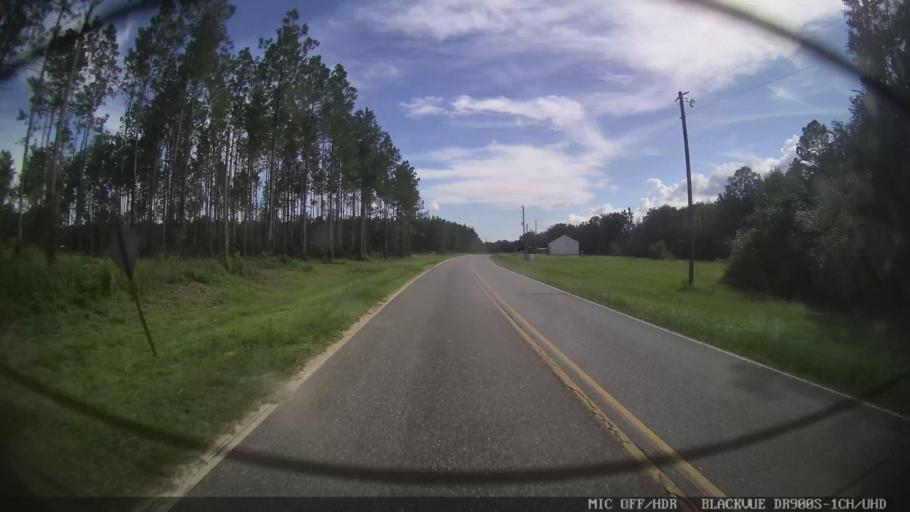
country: US
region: Georgia
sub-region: Echols County
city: Statenville
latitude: 30.6026
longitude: -83.2224
